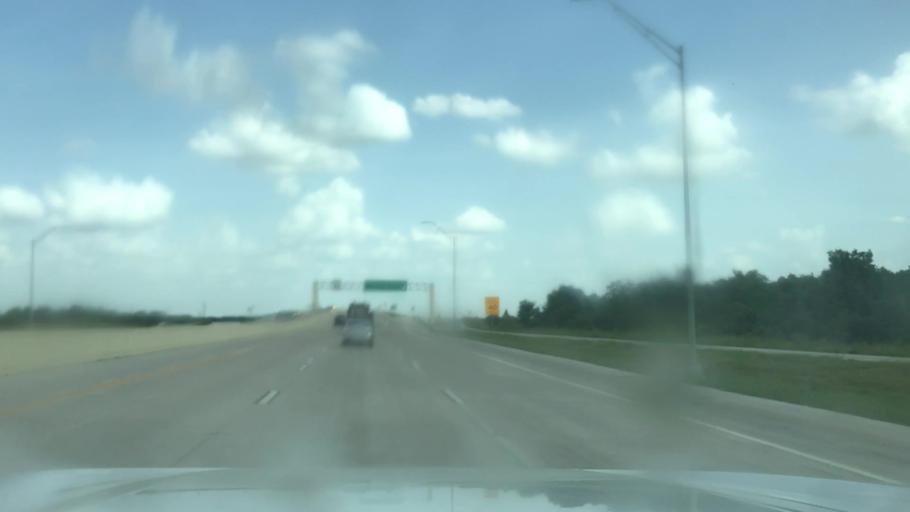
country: US
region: Texas
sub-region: Waller County
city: Waller
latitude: 30.0593
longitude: -95.8970
